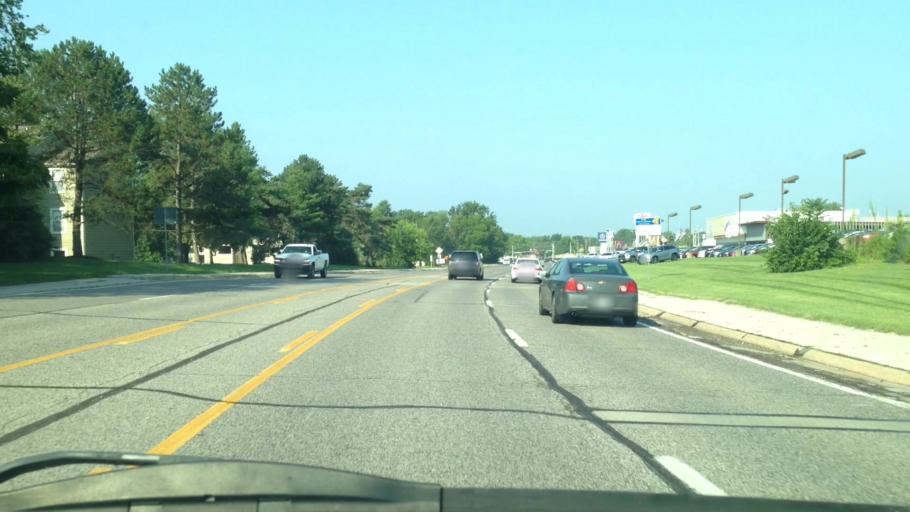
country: US
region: Missouri
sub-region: Saint Louis County
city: Concord
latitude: 38.5217
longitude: -90.3568
